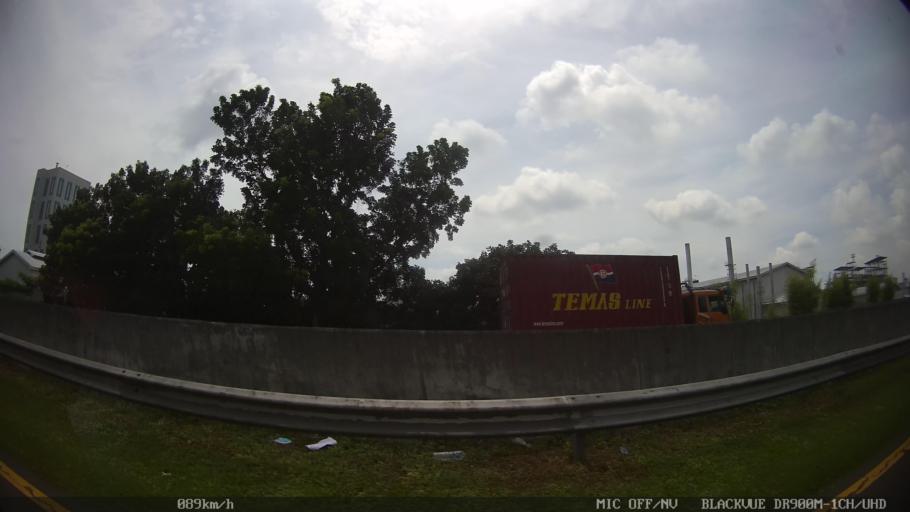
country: ID
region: North Sumatra
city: Labuhan Deli
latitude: 3.6830
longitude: 98.6810
